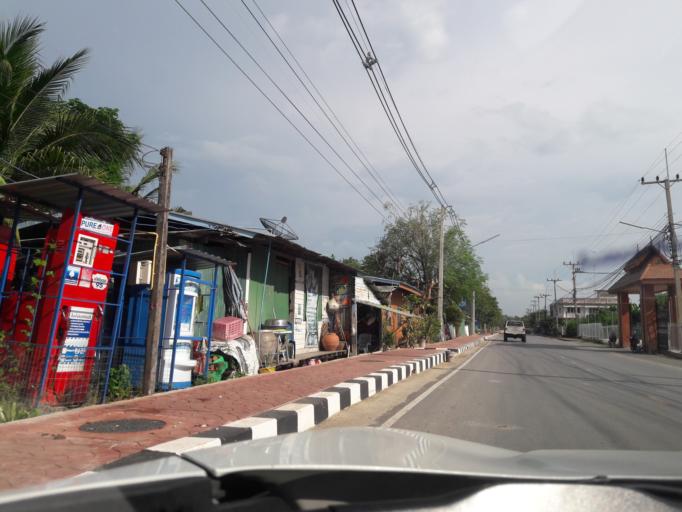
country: TH
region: Lop Buri
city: Ban Mi
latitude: 15.0383
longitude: 100.5403
